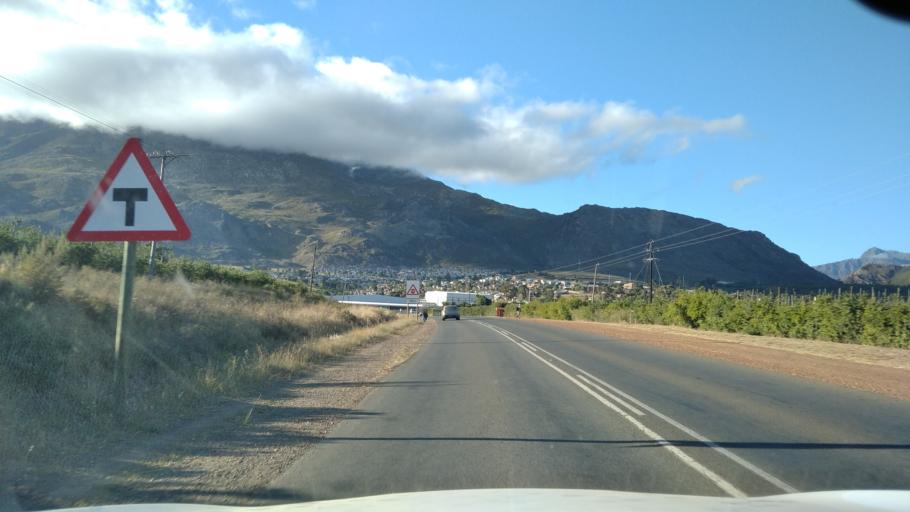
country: ZA
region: Western Cape
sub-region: Overberg District Municipality
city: Caledon
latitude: -33.9995
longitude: 19.2877
